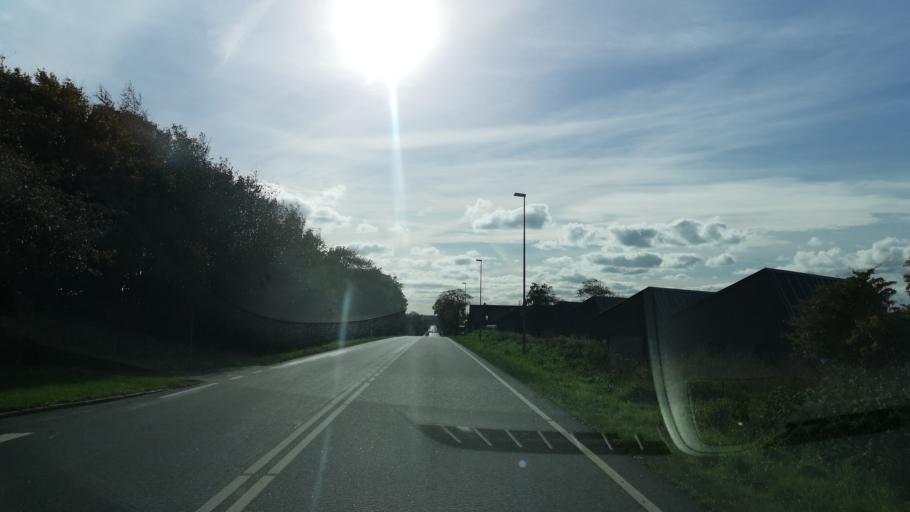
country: DK
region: Central Jutland
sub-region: Holstebro Kommune
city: Holstebro
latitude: 56.3756
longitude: 8.6383
